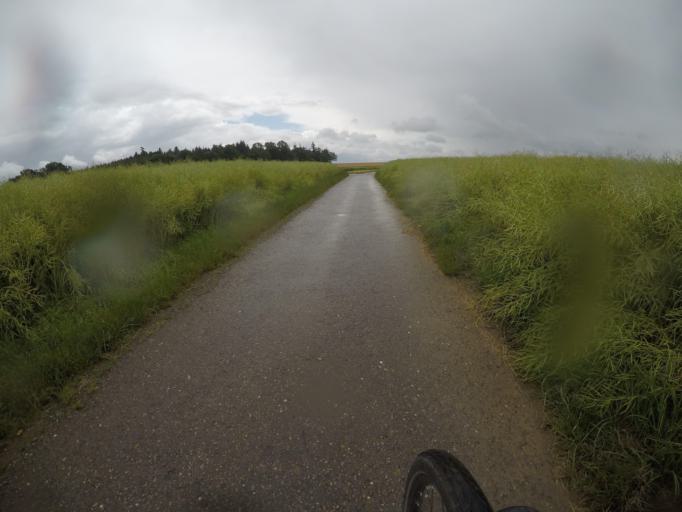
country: DE
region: Baden-Wuerttemberg
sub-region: Regierungsbezirk Stuttgart
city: Motzingen
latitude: 48.5248
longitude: 8.7857
